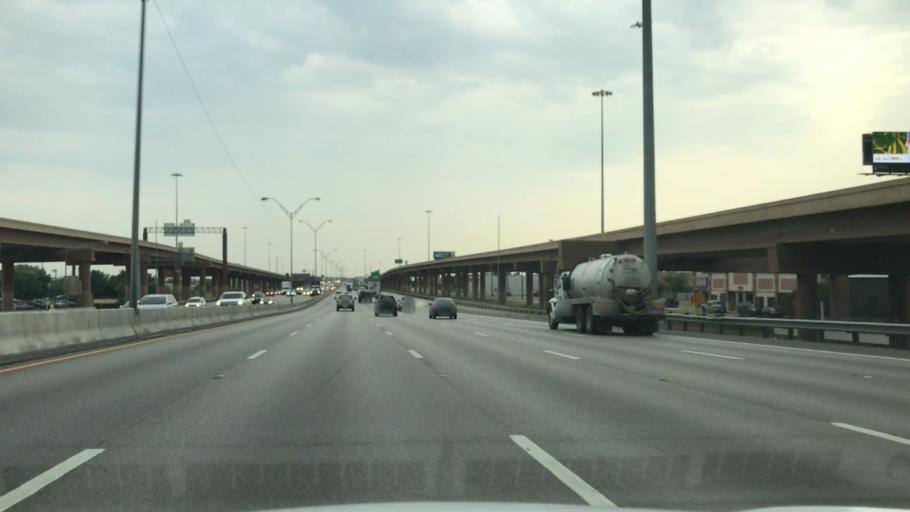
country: US
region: Texas
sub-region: Dallas County
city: Farmers Branch
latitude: 32.8950
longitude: -96.8982
